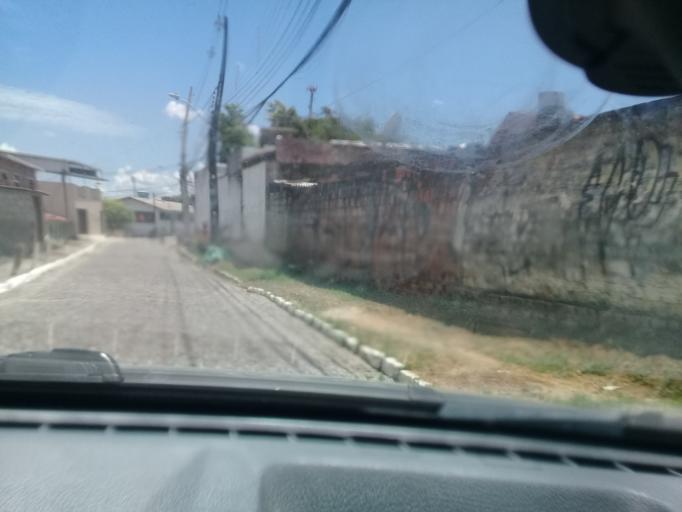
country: BR
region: Pernambuco
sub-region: Jaboatao Dos Guararapes
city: Jaboatao dos Guararapes
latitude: -8.1266
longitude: -34.9530
